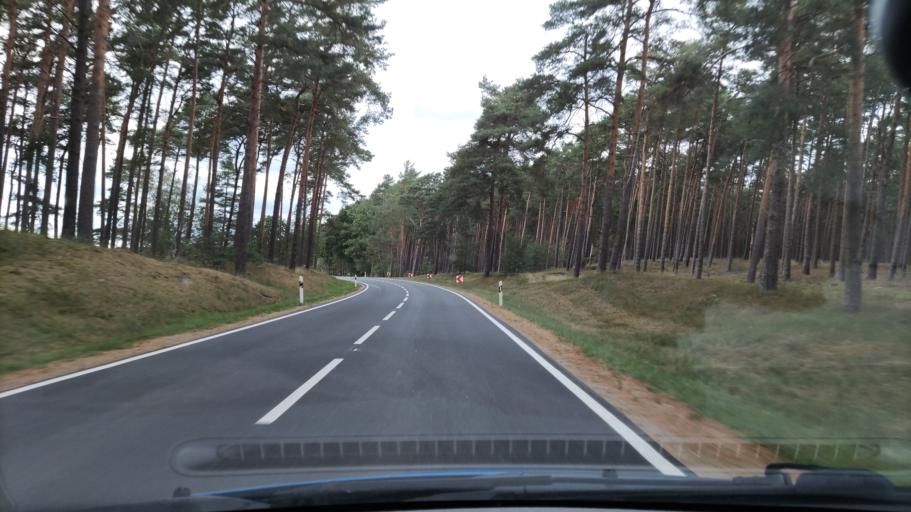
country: DE
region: Lower Saxony
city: Hitzacker
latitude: 53.2152
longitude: 11.0183
